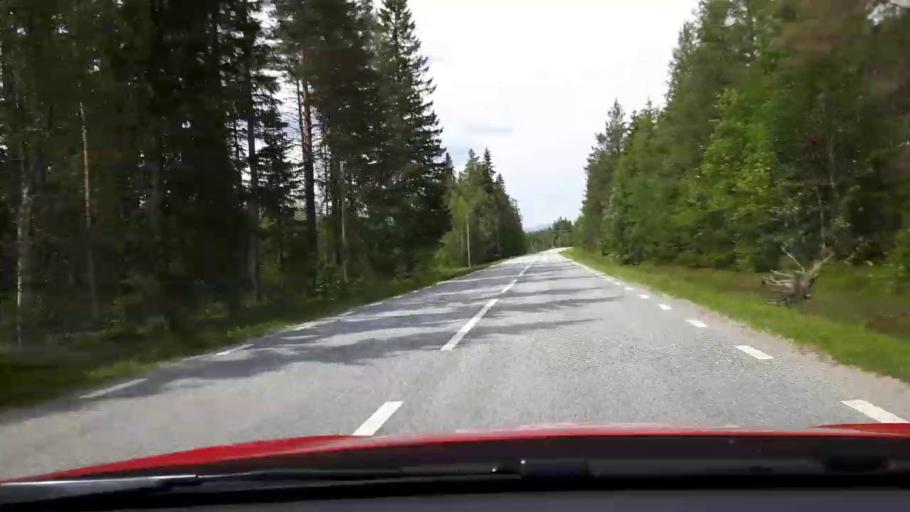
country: SE
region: Jaemtland
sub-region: Harjedalens Kommun
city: Sveg
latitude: 62.1485
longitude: 13.9085
